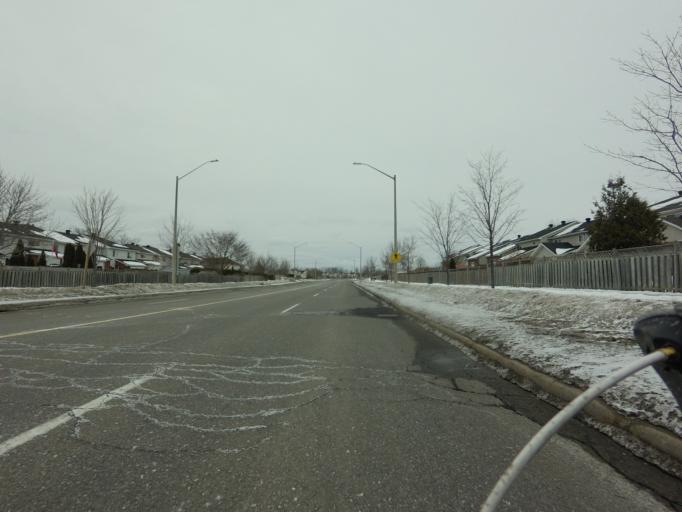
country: CA
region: Ontario
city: Ottawa
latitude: 45.2787
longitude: -75.6874
